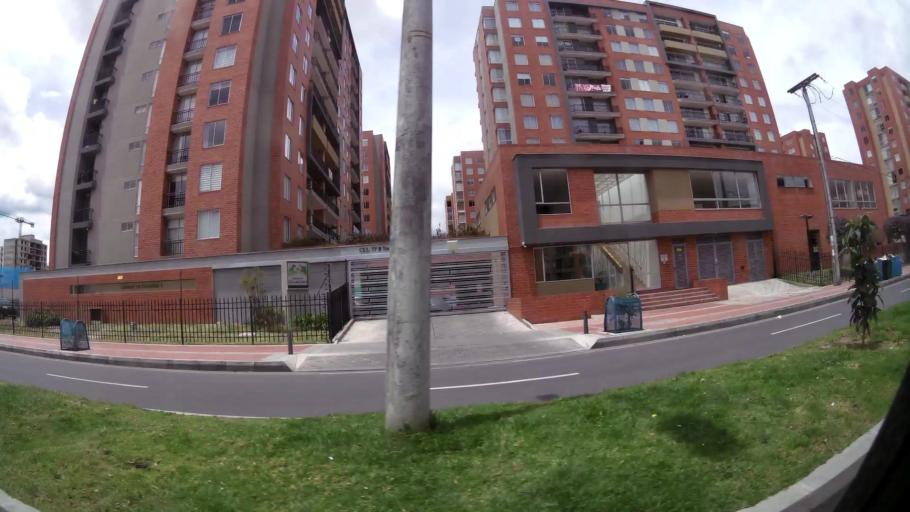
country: CO
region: Cundinamarca
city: Funza
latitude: 4.7225
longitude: -74.1314
